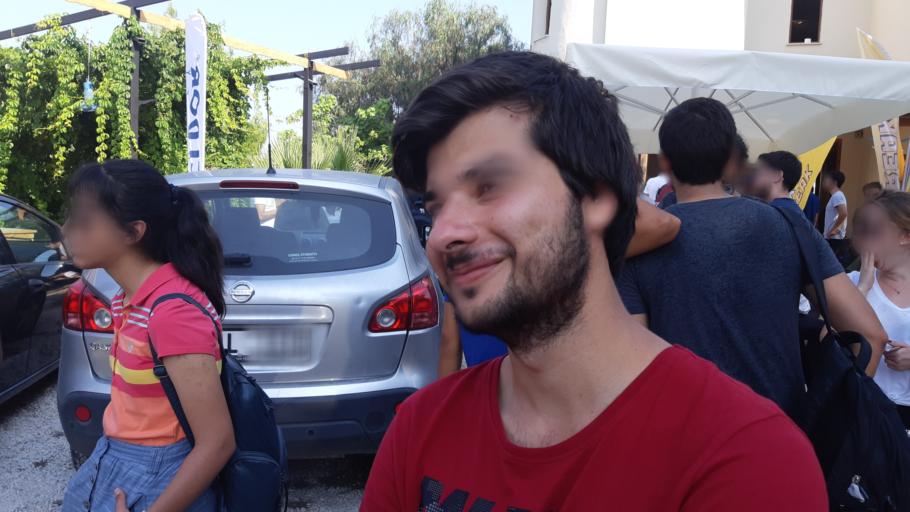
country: TR
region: Izmir
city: Urla
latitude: 38.3246
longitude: 26.7297
